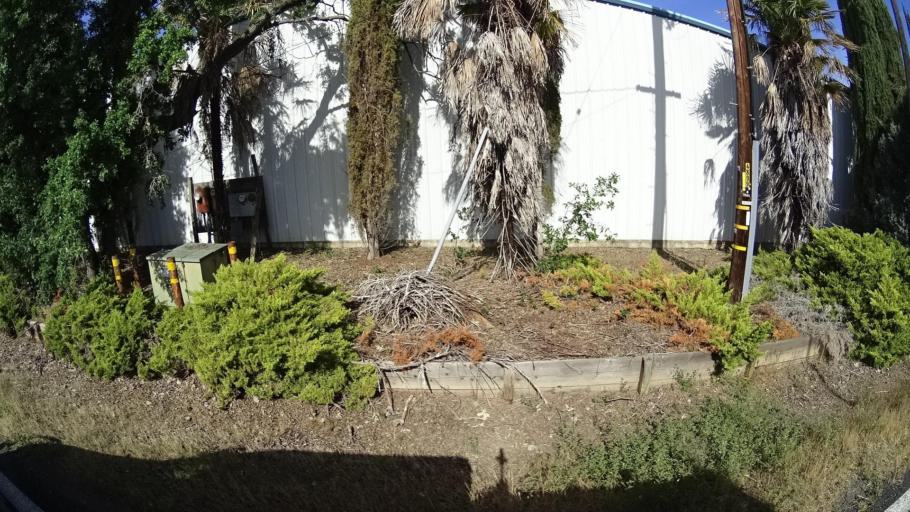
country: US
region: California
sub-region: Lake County
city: Kelseyville
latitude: 38.9890
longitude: -122.8942
